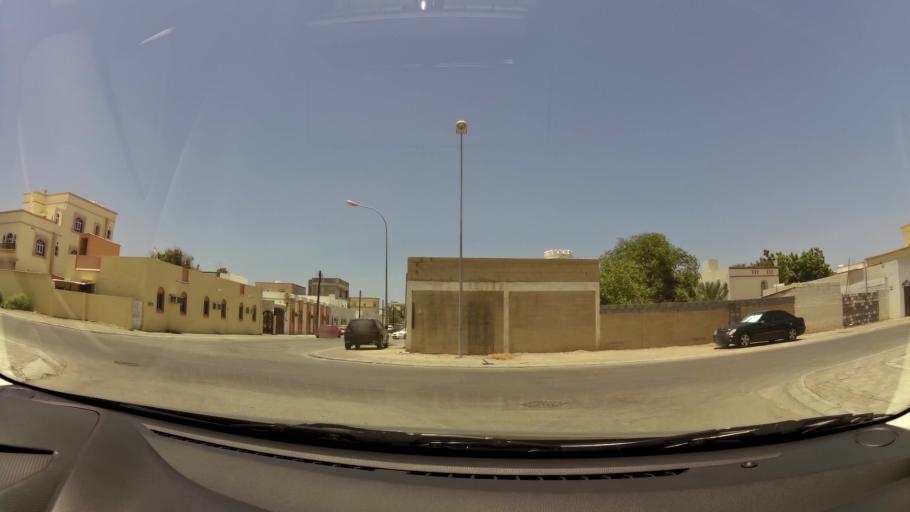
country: OM
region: Muhafazat Masqat
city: Bawshar
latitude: 23.6003
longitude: 58.3904
